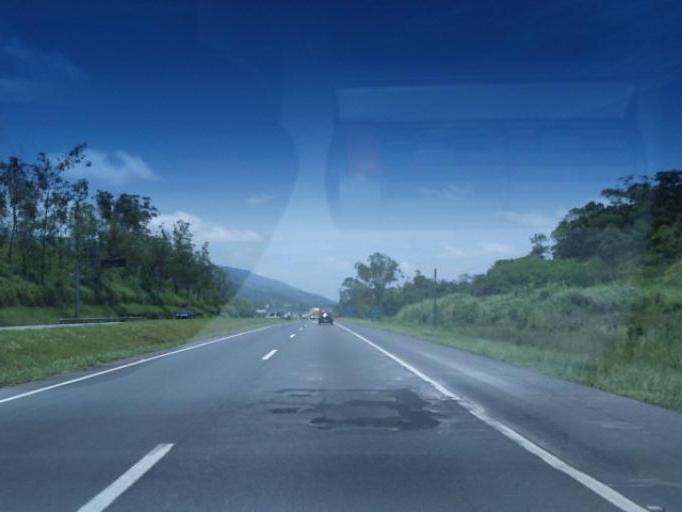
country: BR
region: Sao Paulo
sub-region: Miracatu
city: Miracatu
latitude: -24.2697
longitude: -47.3993
